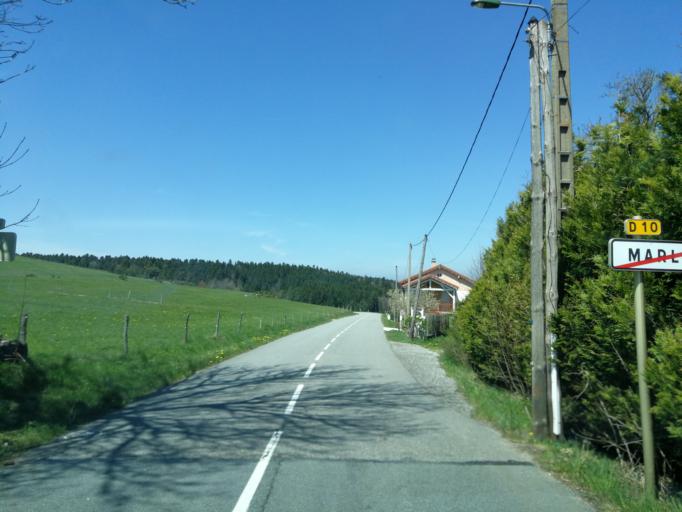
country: FR
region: Rhone-Alpes
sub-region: Departement de la Loire
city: Marlhes
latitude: 45.2857
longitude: 4.3897
